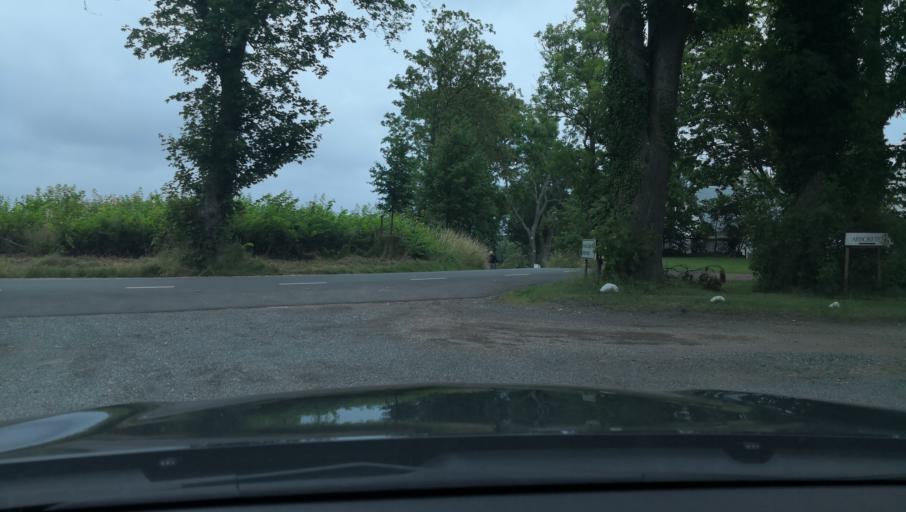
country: SE
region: Skane
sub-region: Simrishamns Kommun
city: Kivik
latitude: 55.6785
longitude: 14.2387
